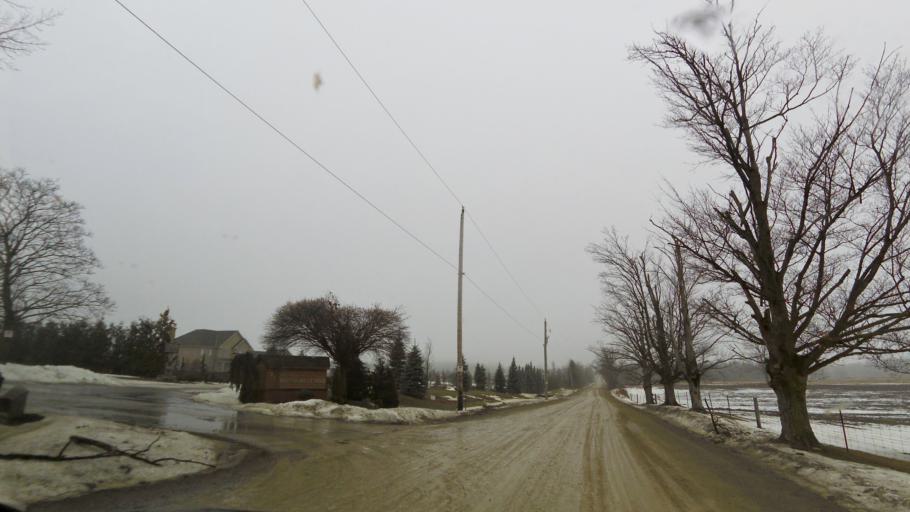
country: CA
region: Ontario
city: Brampton
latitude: 43.8362
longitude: -79.8577
